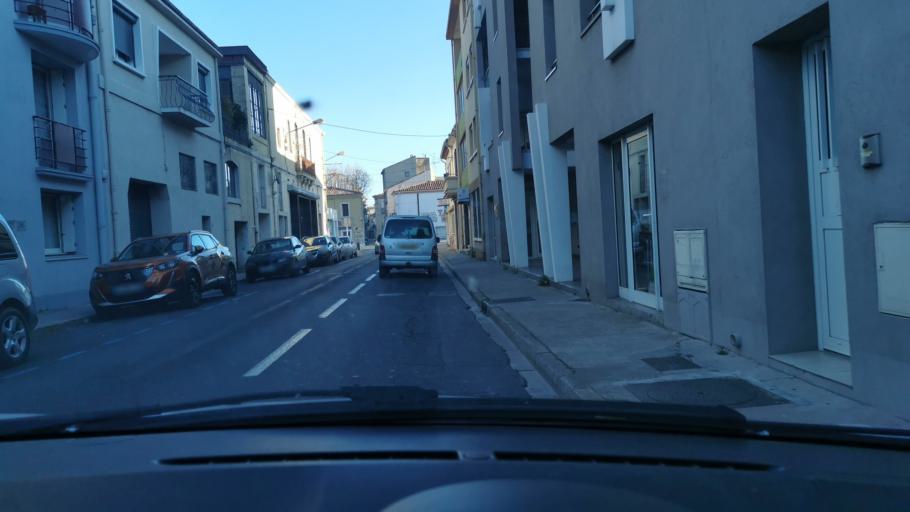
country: FR
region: Languedoc-Roussillon
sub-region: Departement de l'Herault
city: Frontignan
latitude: 43.4474
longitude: 3.7532
